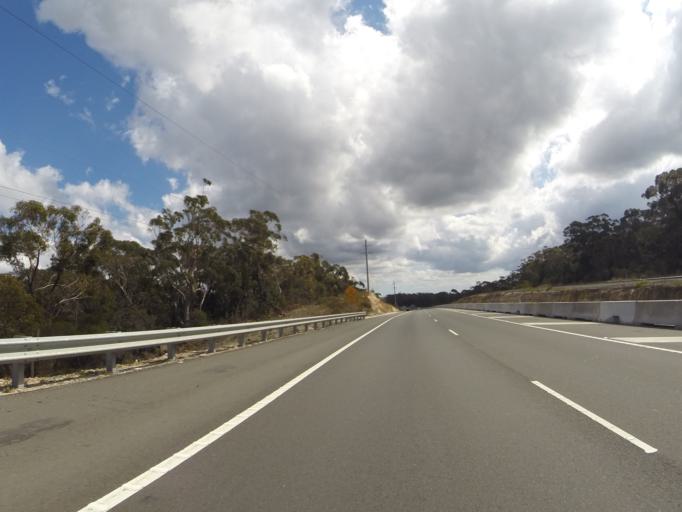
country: AU
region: New South Wales
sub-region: Wollongong
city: Mount Keira
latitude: -34.3592
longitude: 150.8125
